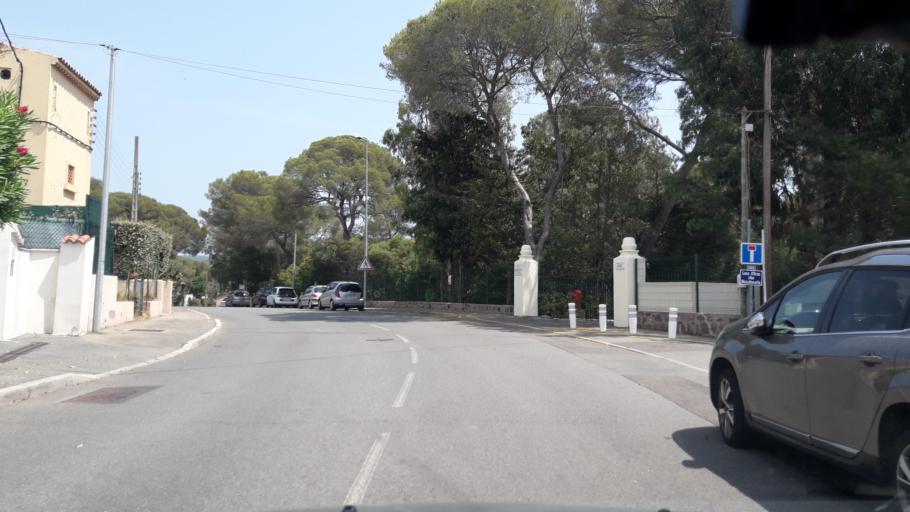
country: FR
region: Provence-Alpes-Cote d'Azur
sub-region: Departement du Var
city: Saint-Raphael
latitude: 43.4196
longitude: 6.8023
